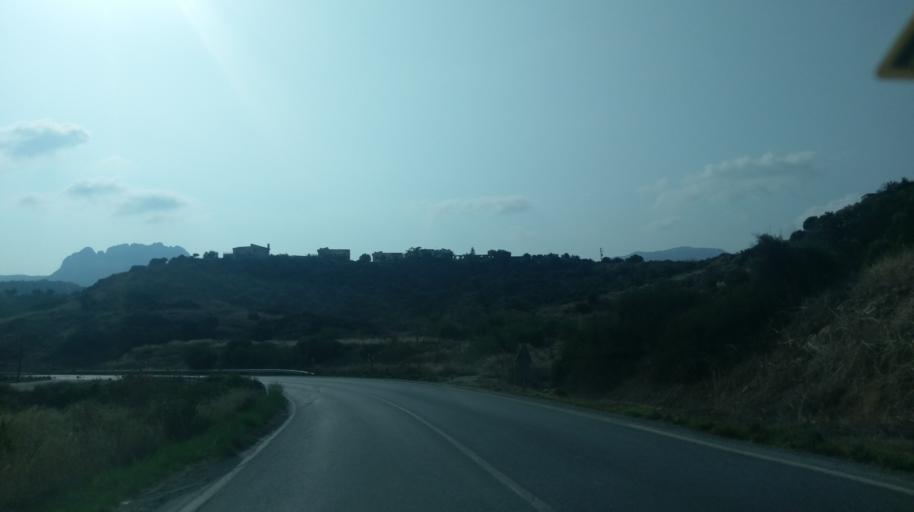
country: CY
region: Keryneia
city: Kyrenia
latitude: 35.3280
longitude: 33.4655
